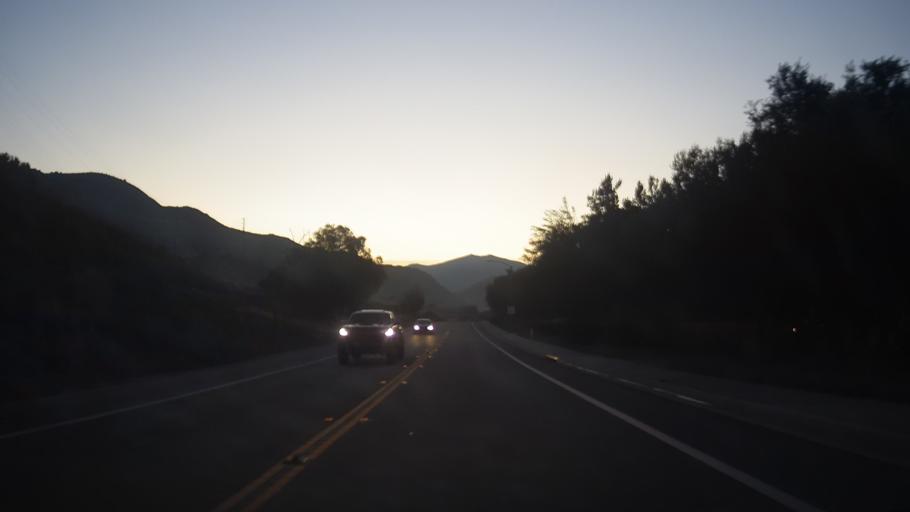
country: US
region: California
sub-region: San Diego County
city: Crest
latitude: 32.7849
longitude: -116.8818
